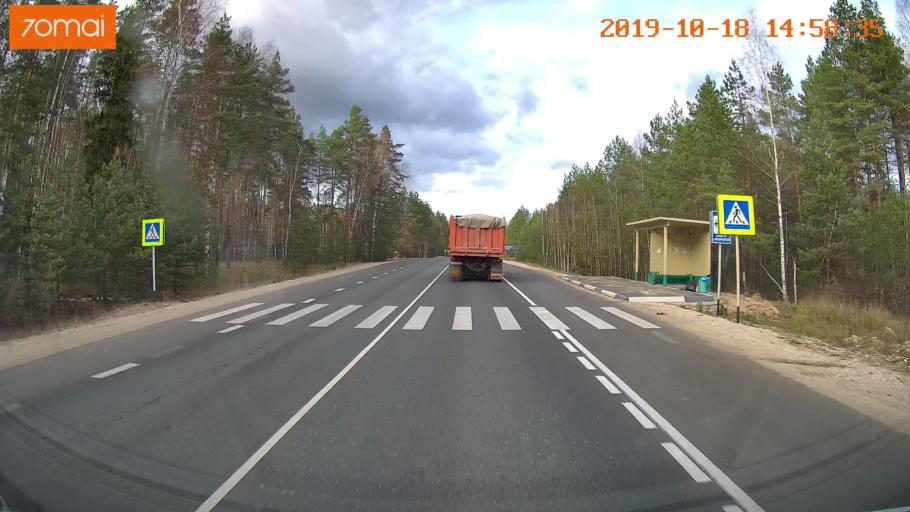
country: RU
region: Vladimir
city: Kurlovo
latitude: 55.4920
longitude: 40.5765
